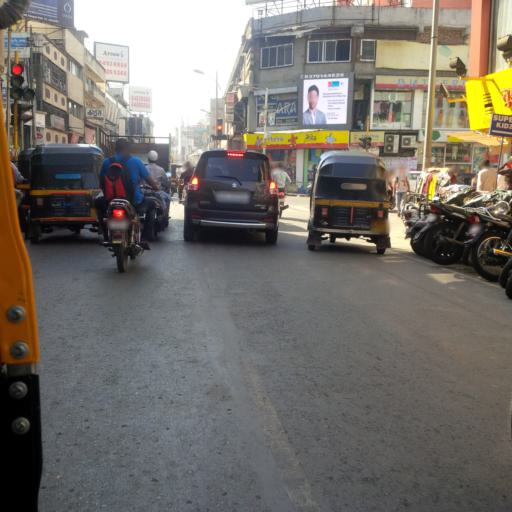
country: IN
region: Maharashtra
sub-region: Pune Division
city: Pune
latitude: 18.5146
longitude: 73.8541
